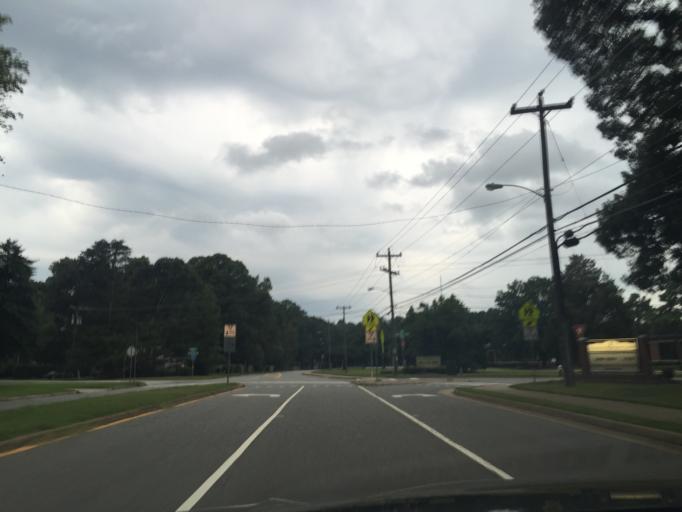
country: US
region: Virginia
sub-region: City of Newport News
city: Newport News
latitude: 37.0658
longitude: -76.5072
